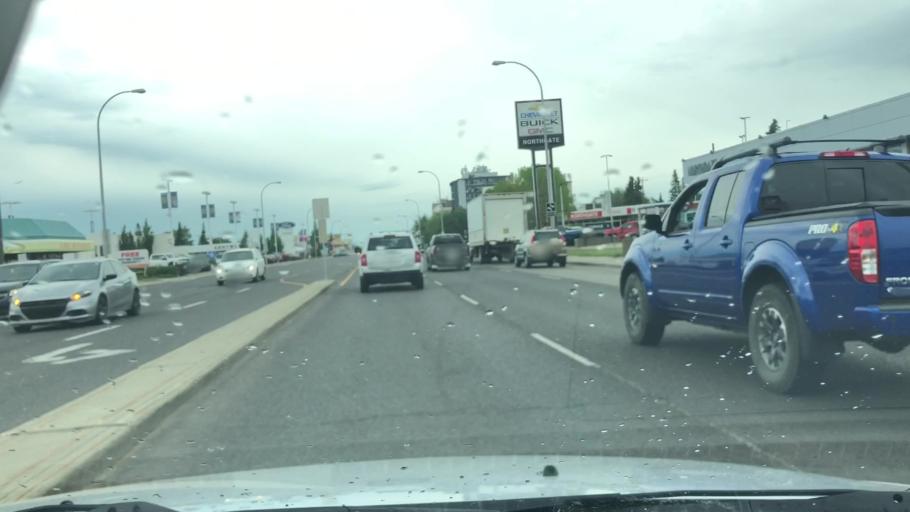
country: CA
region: Alberta
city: Edmonton
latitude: 53.5925
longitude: -113.4920
